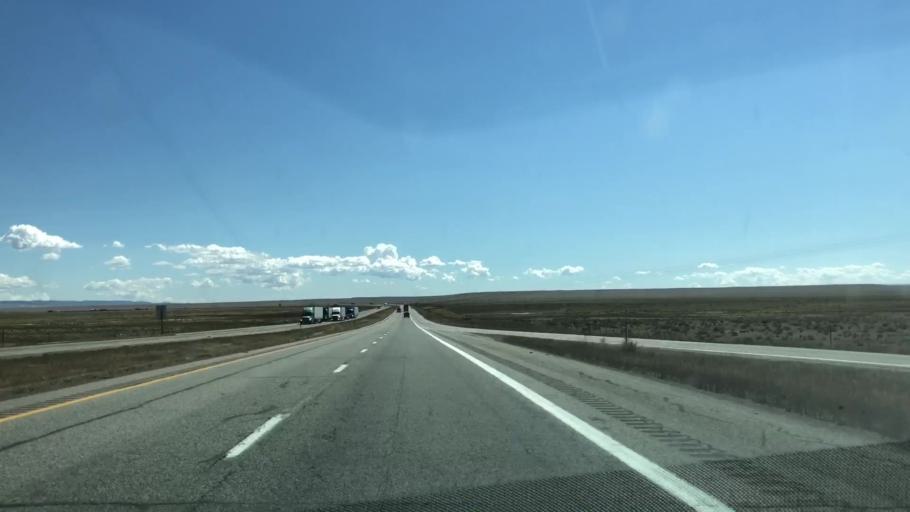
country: US
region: Wyoming
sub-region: Albany County
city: Laramie
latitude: 41.3928
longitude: -105.8225
